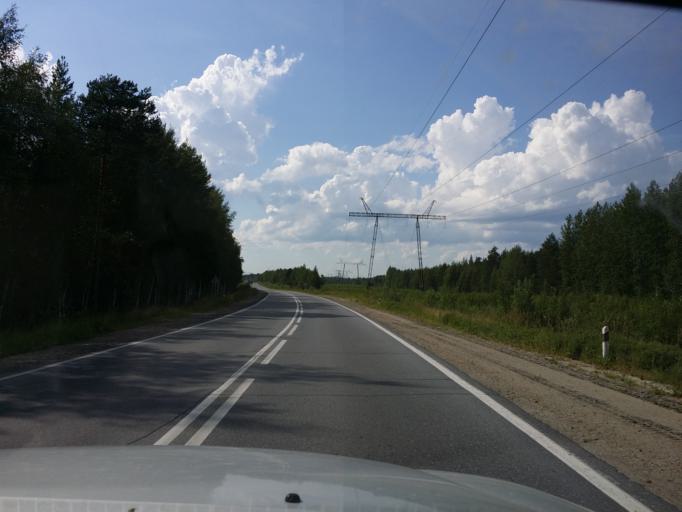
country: RU
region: Khanty-Mansiyskiy Avtonomnyy Okrug
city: Megion
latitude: 61.1600
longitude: 75.7258
